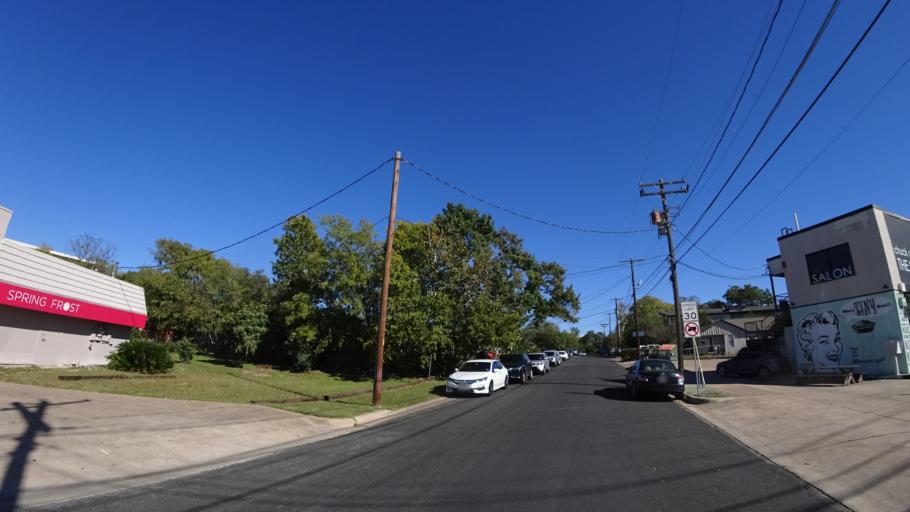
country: US
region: Texas
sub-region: Travis County
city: Austin
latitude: 30.3225
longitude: -97.7392
